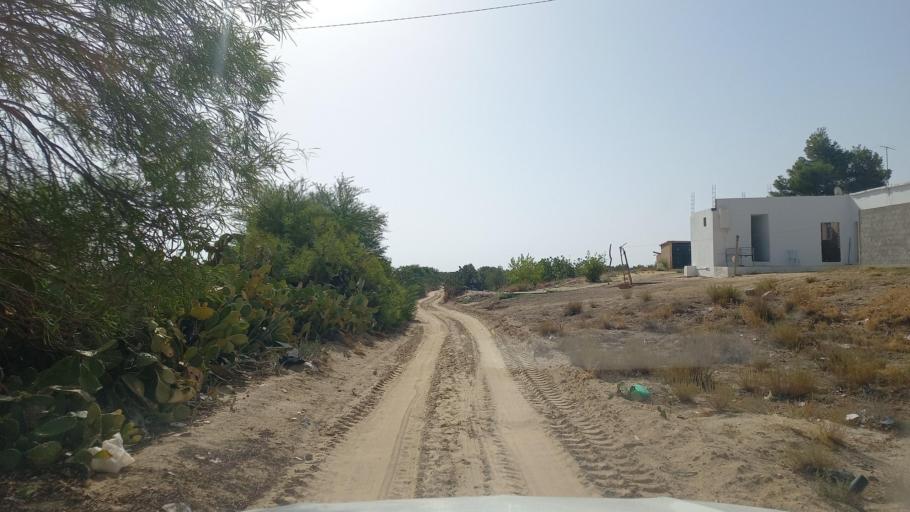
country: TN
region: Al Qasrayn
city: Kasserine
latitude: 35.2525
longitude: 9.0272
